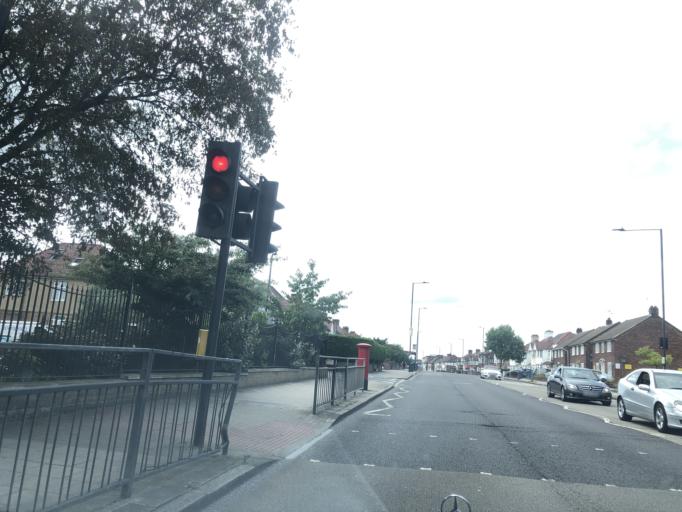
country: GB
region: England
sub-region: Greater London
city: Edgware
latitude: 51.5864
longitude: -0.2928
